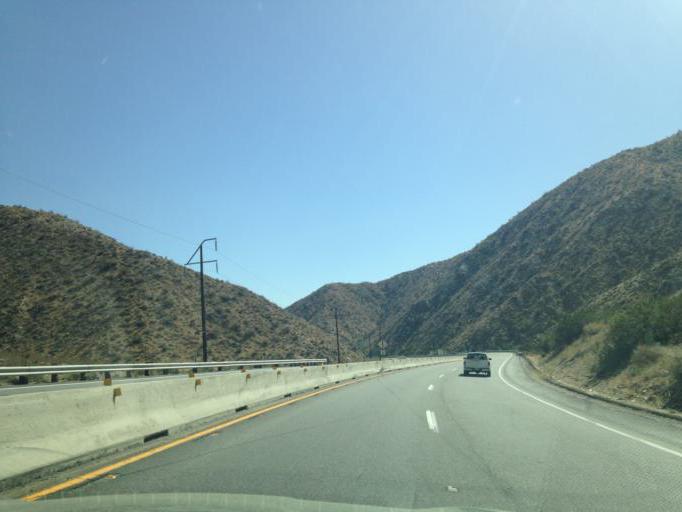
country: US
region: California
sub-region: San Bernardino County
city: Morongo Valley
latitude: 34.0265
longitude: -116.5852
